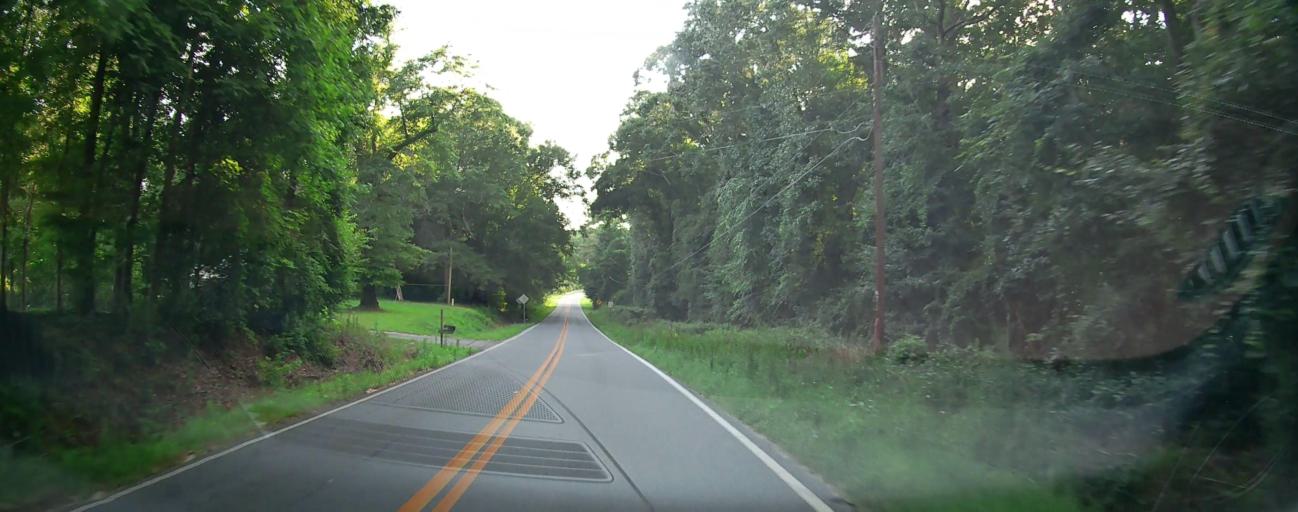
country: US
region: Georgia
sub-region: Peach County
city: Byron
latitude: 32.7178
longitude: -83.7481
